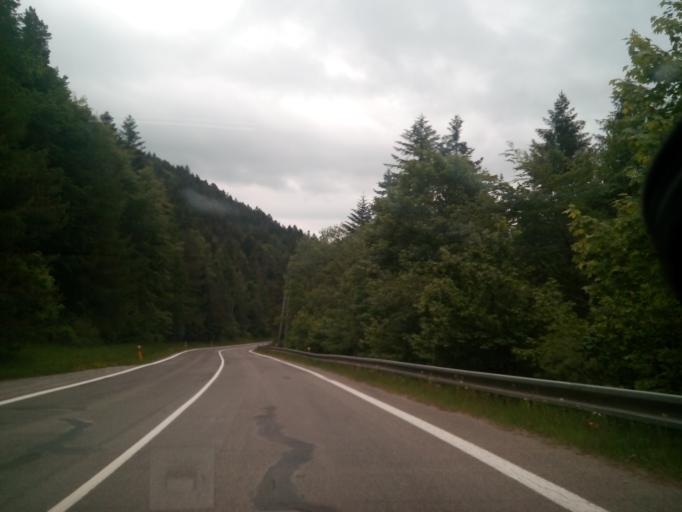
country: SK
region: Kosicky
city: Krompachy
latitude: 48.9987
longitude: 20.8827
